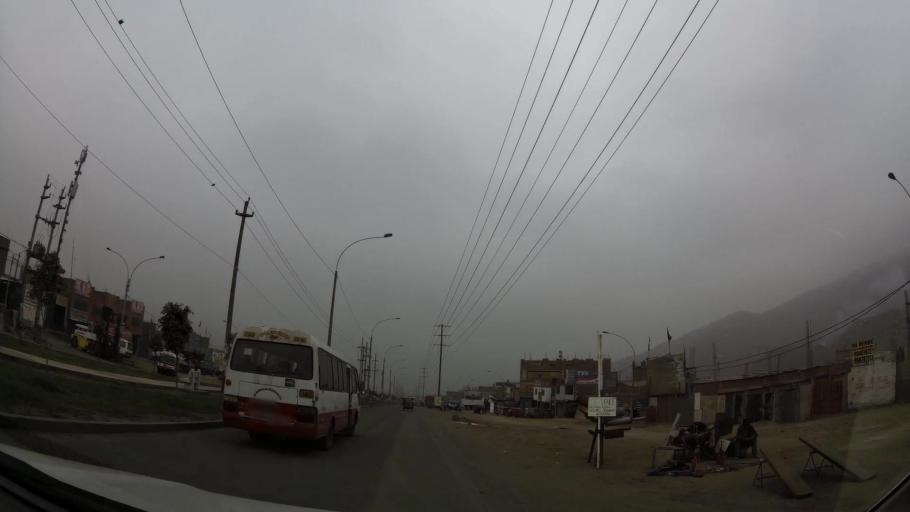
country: PE
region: Lima
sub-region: Lima
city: Urb. Santo Domingo
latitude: -11.9259
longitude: -76.9639
